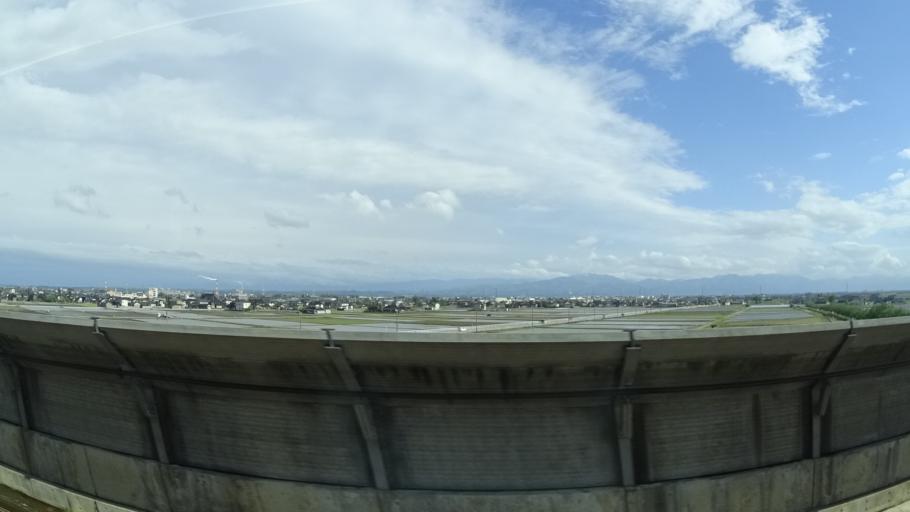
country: JP
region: Toyama
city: Takaoka
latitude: 36.7214
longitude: 136.9827
